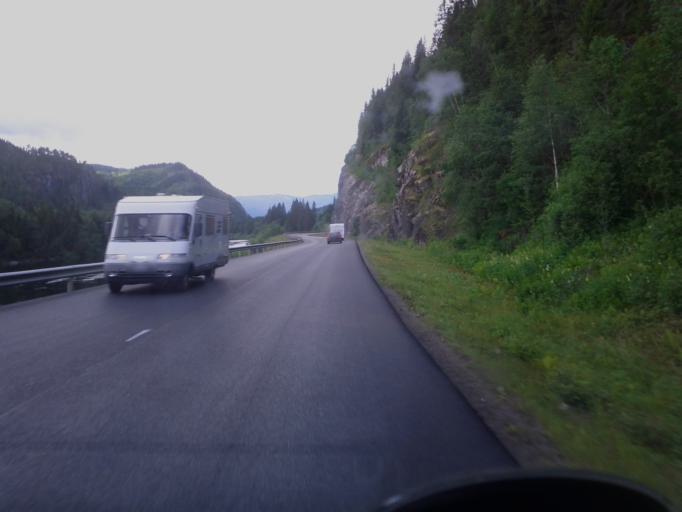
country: NO
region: Nord-Trondelag
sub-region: Grong
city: Grong
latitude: 64.5224
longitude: 12.3830
